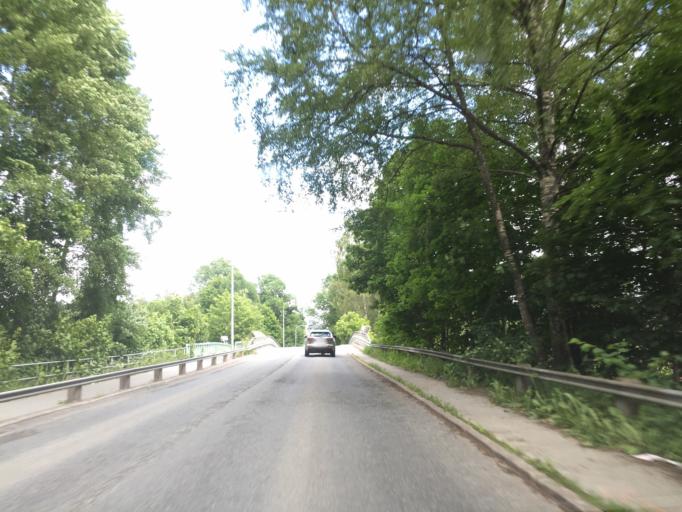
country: SE
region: OErebro
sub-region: Orebro Kommun
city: Orebro
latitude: 59.2405
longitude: 15.1689
